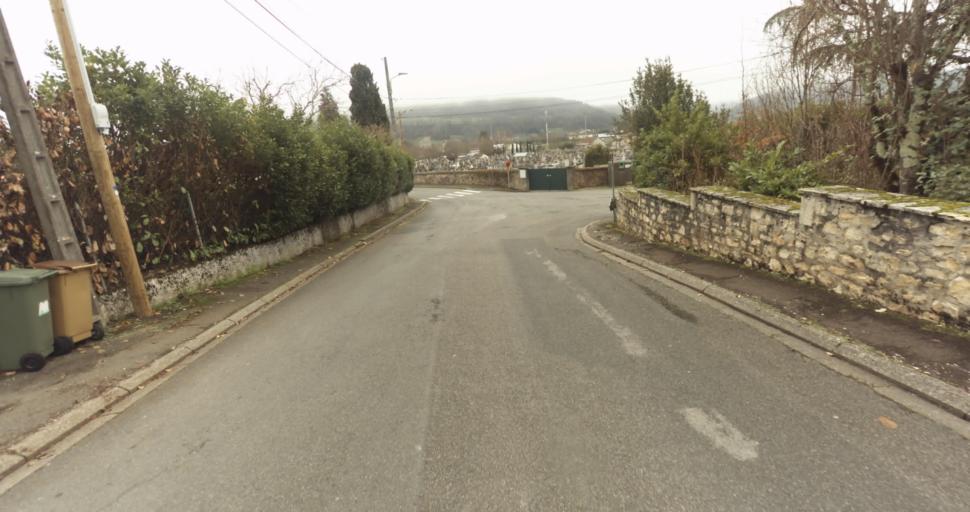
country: FR
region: Midi-Pyrenees
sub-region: Departement du Lot
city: Figeac
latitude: 44.6143
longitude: 2.0344
